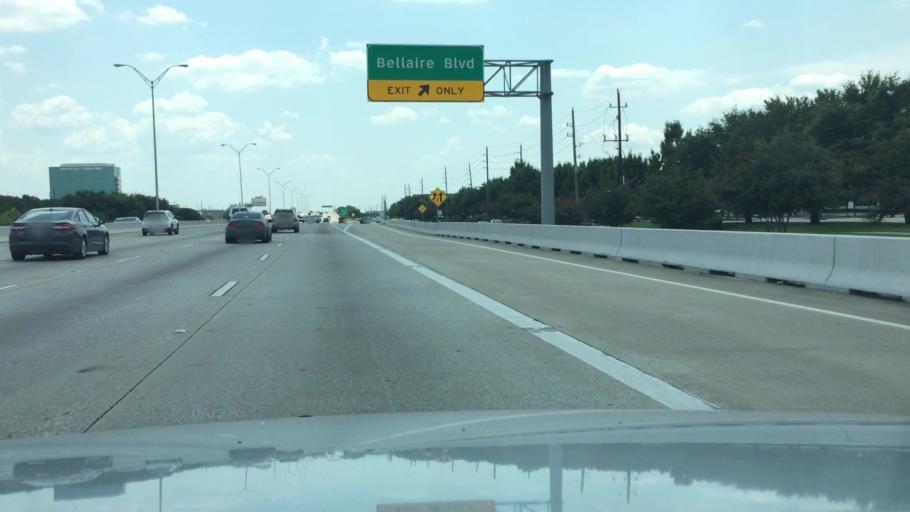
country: US
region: Texas
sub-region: Harris County
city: Bunker Hill Village
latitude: 29.7119
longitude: -95.5577
